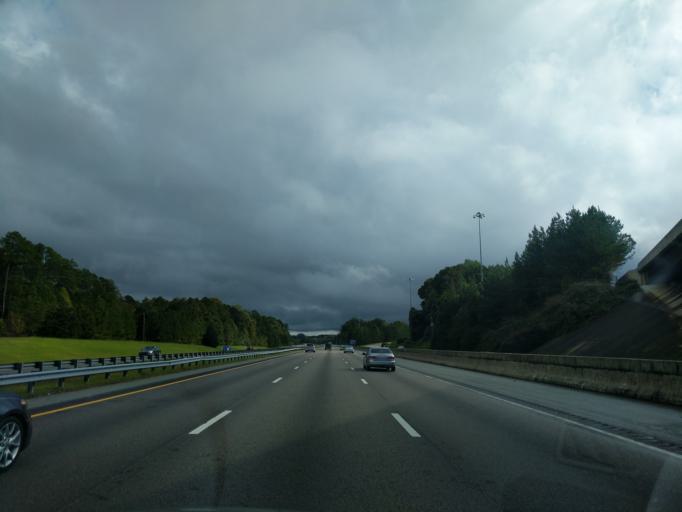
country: US
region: North Carolina
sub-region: Durham County
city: Durham
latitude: 36.0318
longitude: -78.9631
